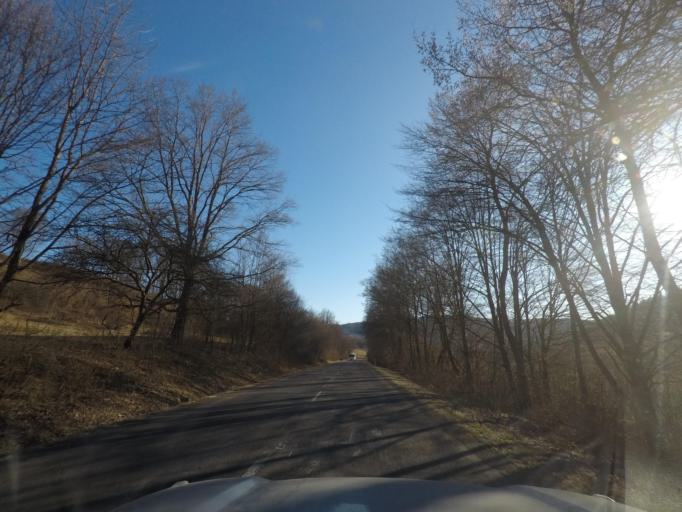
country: SK
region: Presovsky
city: Medzilaborce
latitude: 49.2628
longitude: 21.7962
